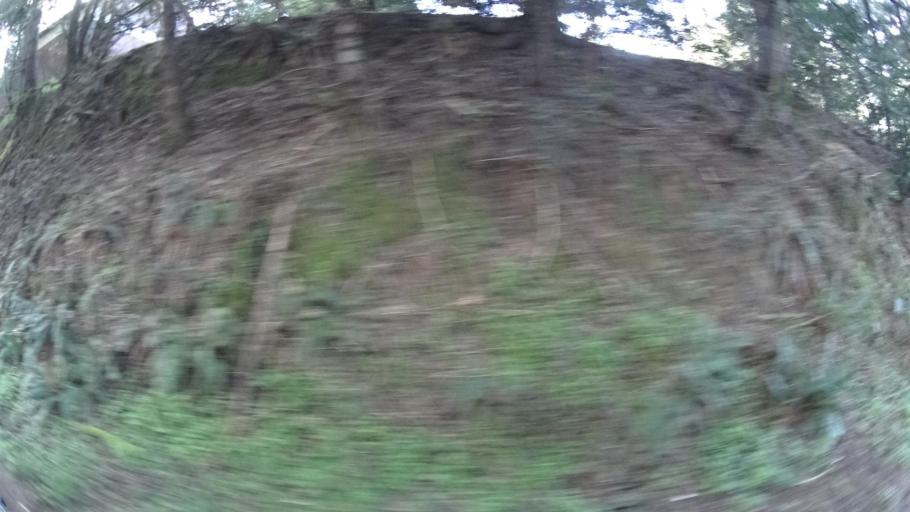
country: US
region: California
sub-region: Humboldt County
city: Blue Lake
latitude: 40.7394
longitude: -123.9572
